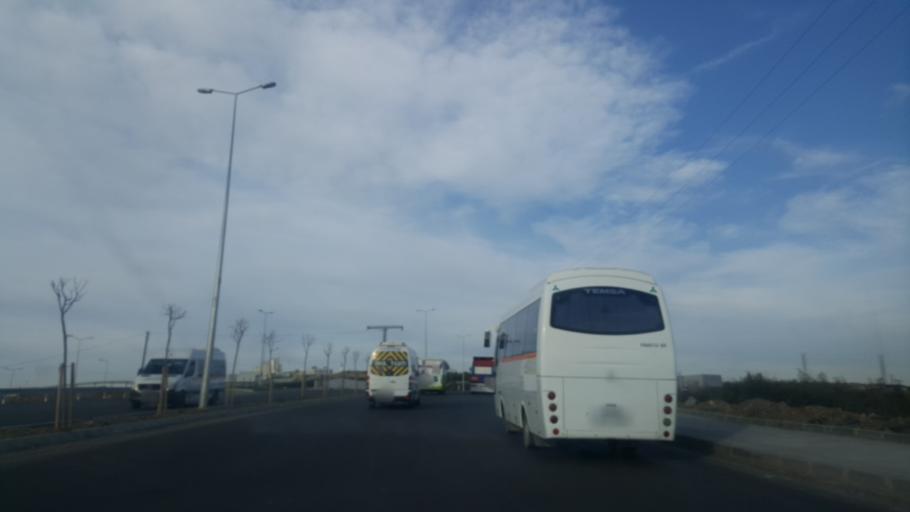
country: TR
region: Kocaeli
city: Tavsancil
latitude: 40.8041
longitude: 29.5517
